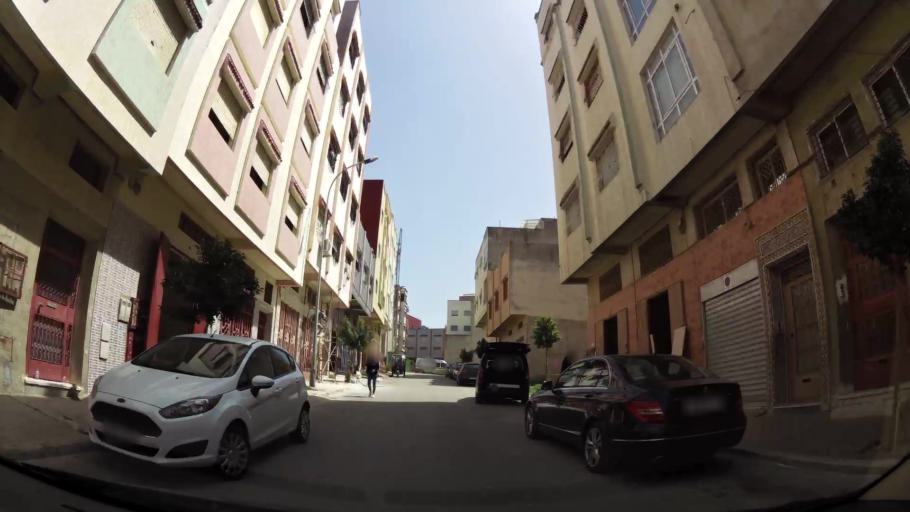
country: MA
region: Tanger-Tetouan
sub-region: Tanger-Assilah
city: Tangier
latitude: 35.7553
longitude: -5.8390
